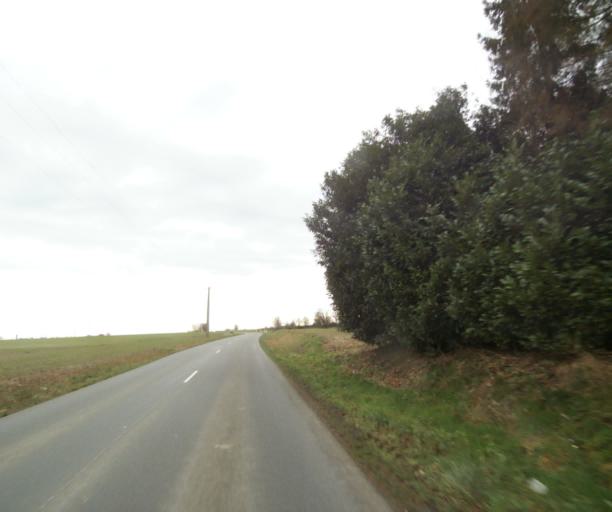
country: FR
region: Nord-Pas-de-Calais
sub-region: Departement du Nord
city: Saultain
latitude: 50.3581
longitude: 3.5935
